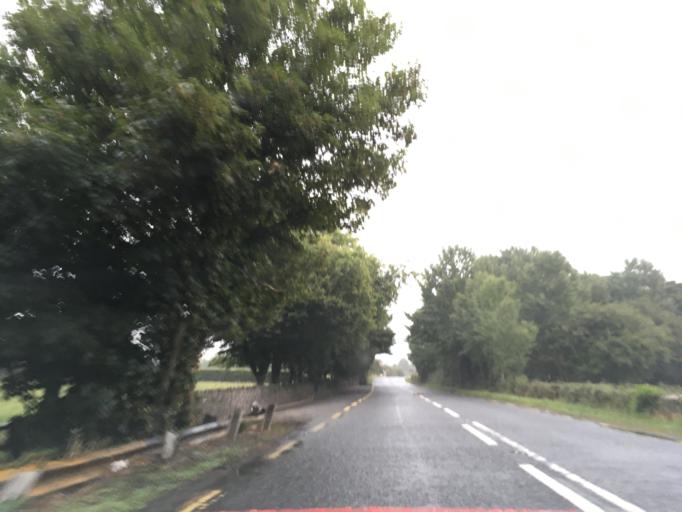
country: IE
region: Munster
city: Tipperary
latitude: 52.4800
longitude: -8.1184
